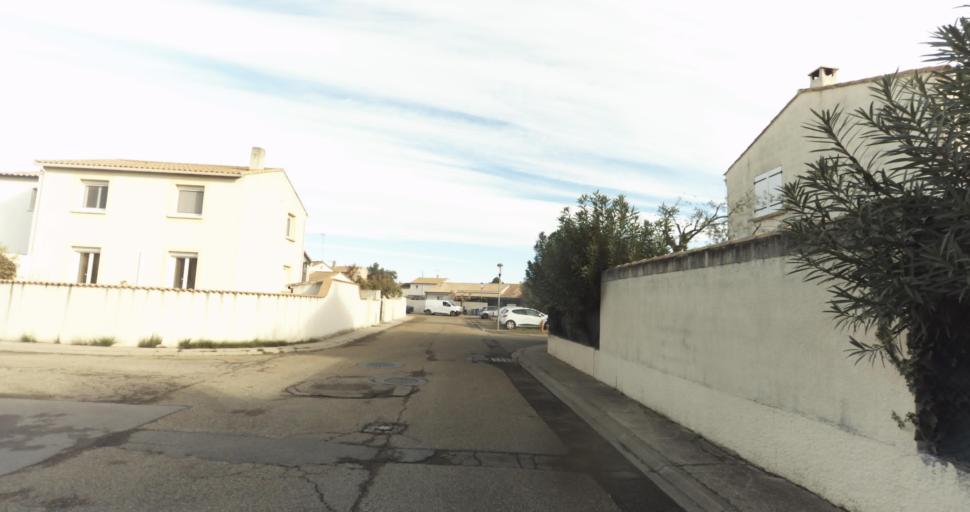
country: FR
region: Languedoc-Roussillon
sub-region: Departement du Gard
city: Aigues-Mortes
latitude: 43.5728
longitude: 4.1986
